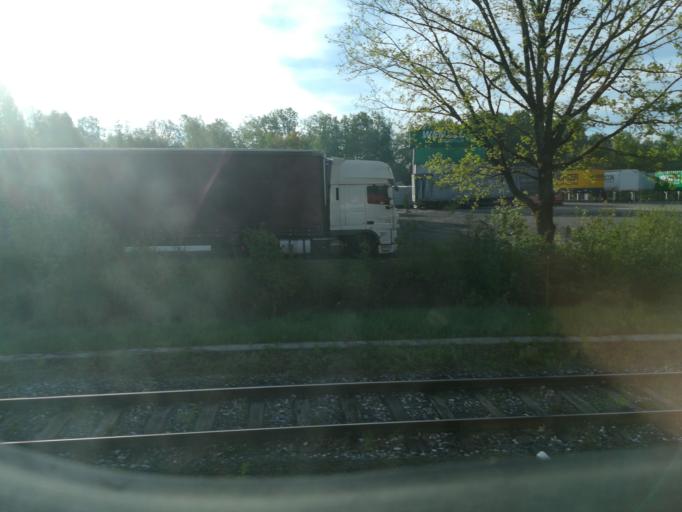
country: AT
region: Styria
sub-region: Politischer Bezirk Graz-Umgebung
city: Unterpremstatten
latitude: 46.9763
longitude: 15.3900
